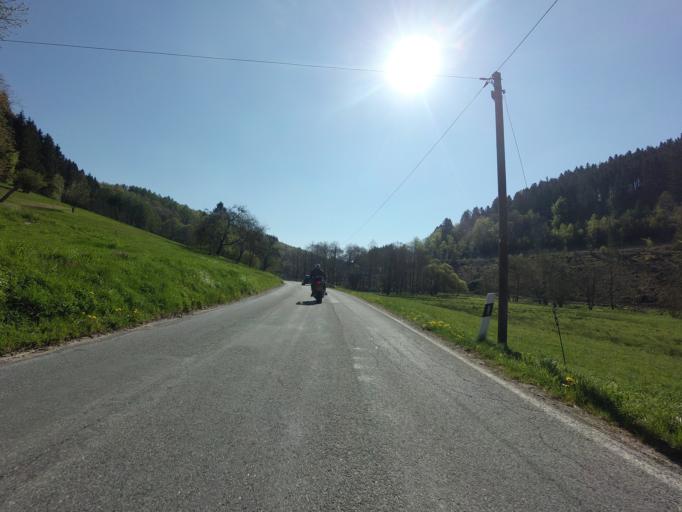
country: DE
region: North Rhine-Westphalia
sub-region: Regierungsbezirk Arnsberg
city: Herscheid
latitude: 51.1033
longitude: 7.7372
